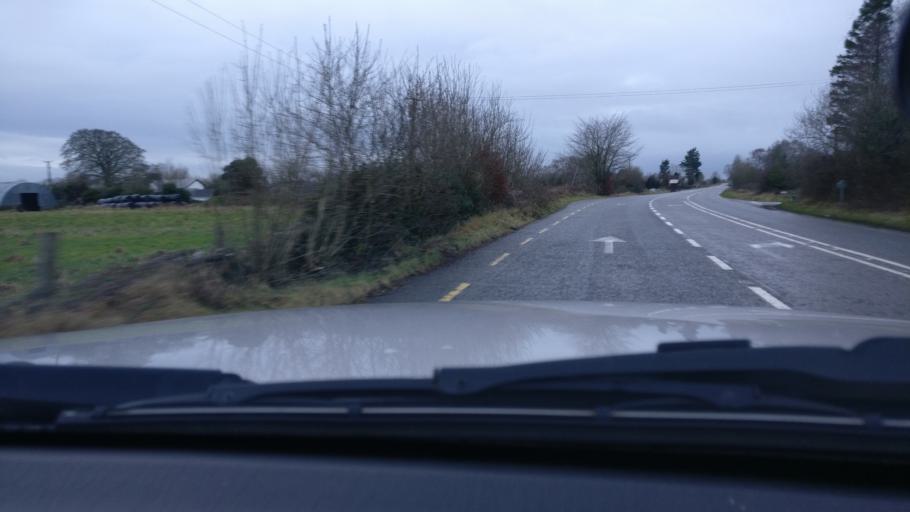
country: IE
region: Leinster
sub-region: An Iarmhi
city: Athlone
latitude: 53.3698
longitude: -8.0240
